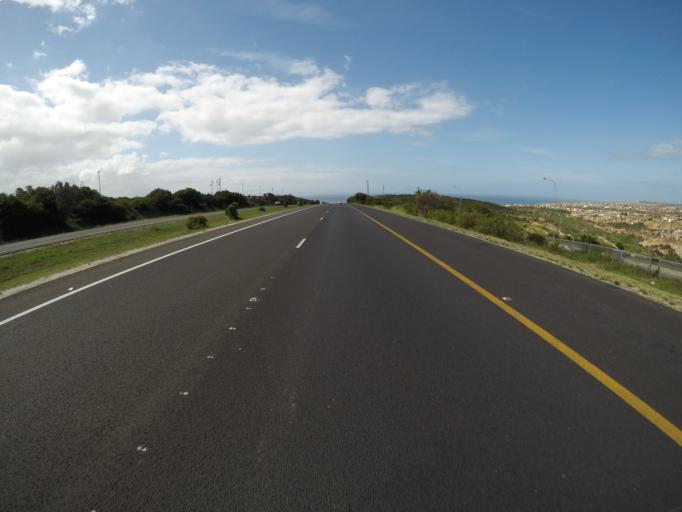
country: ZA
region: Western Cape
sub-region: Eden District Municipality
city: Mossel Bay
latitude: -34.1641
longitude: 22.0897
